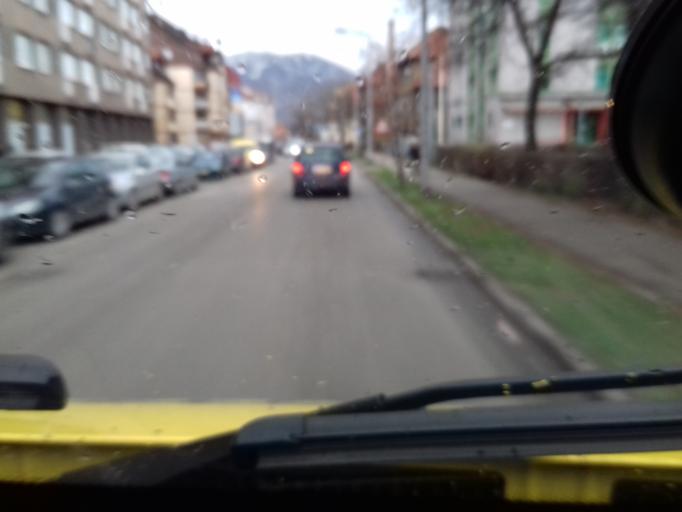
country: BA
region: Federation of Bosnia and Herzegovina
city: Zenica
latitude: 44.2085
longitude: 17.9075
